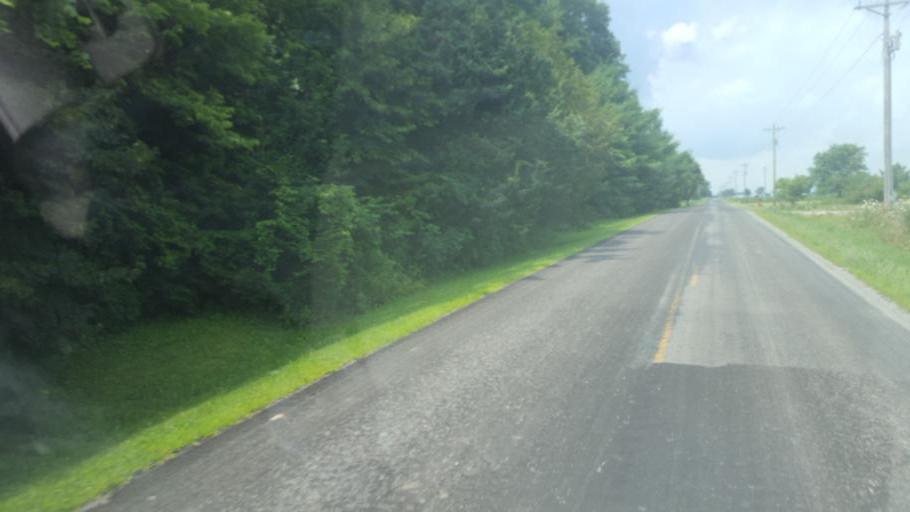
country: US
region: Ohio
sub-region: Hardin County
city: Kenton
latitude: 40.5837
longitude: -83.5117
